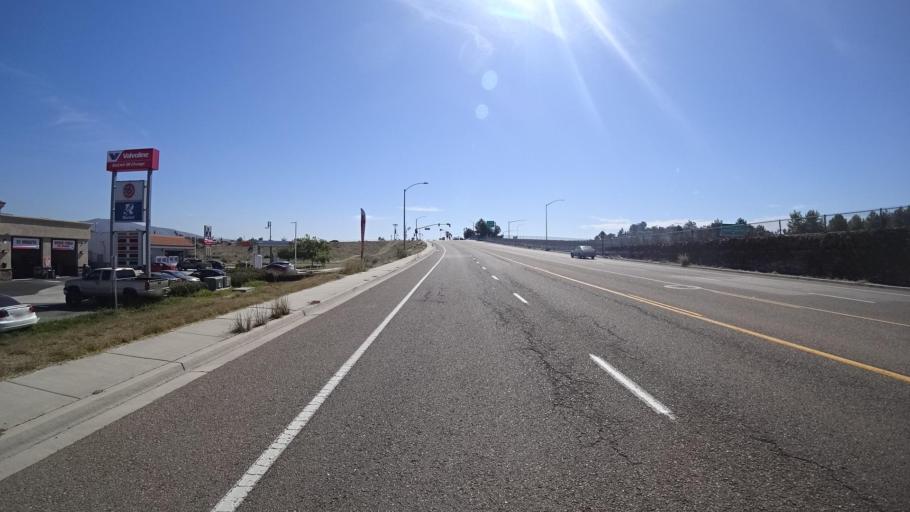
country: US
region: California
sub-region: San Diego County
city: La Presa
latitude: 32.7068
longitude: -117.0108
